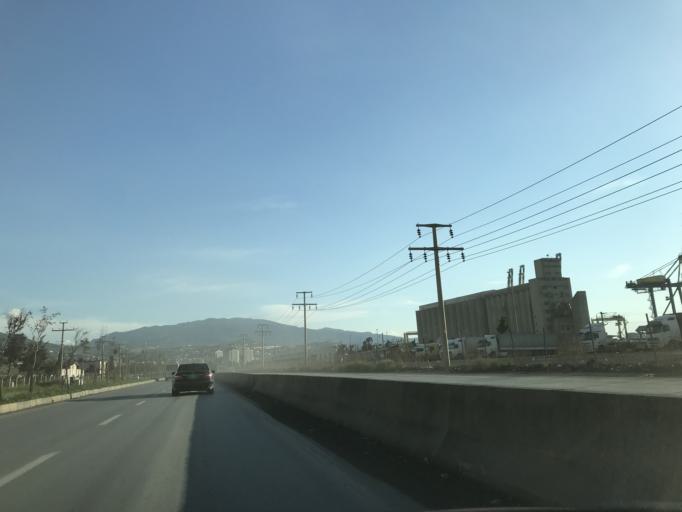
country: TR
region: Hatay
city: Iskenderun
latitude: 36.5997
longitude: 36.1969
